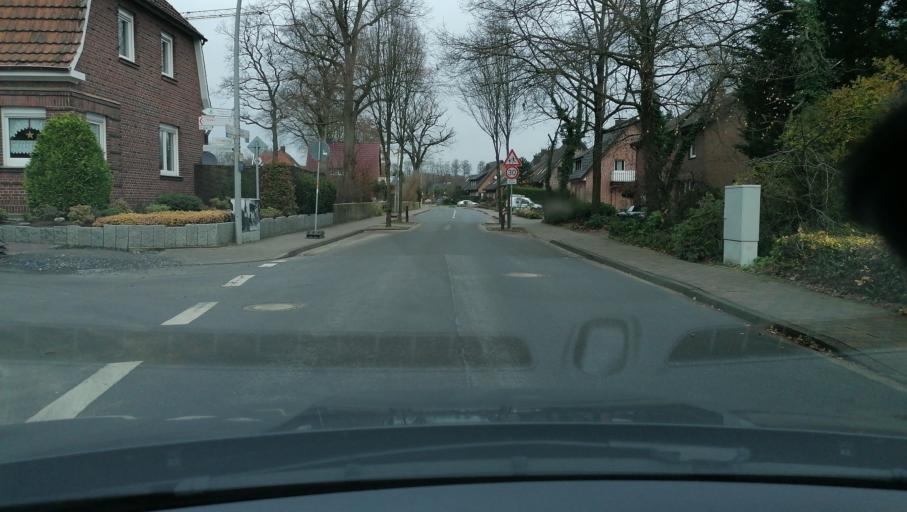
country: DE
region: North Rhine-Westphalia
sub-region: Regierungsbezirk Munster
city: Klein Reken
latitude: 51.7876
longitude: 7.0384
